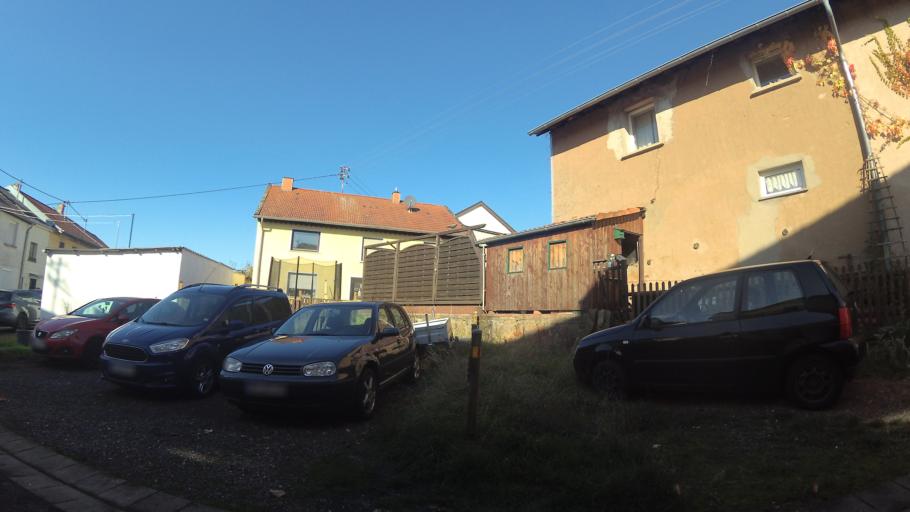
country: DE
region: Saarland
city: Britten
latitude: 49.5314
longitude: 6.6961
